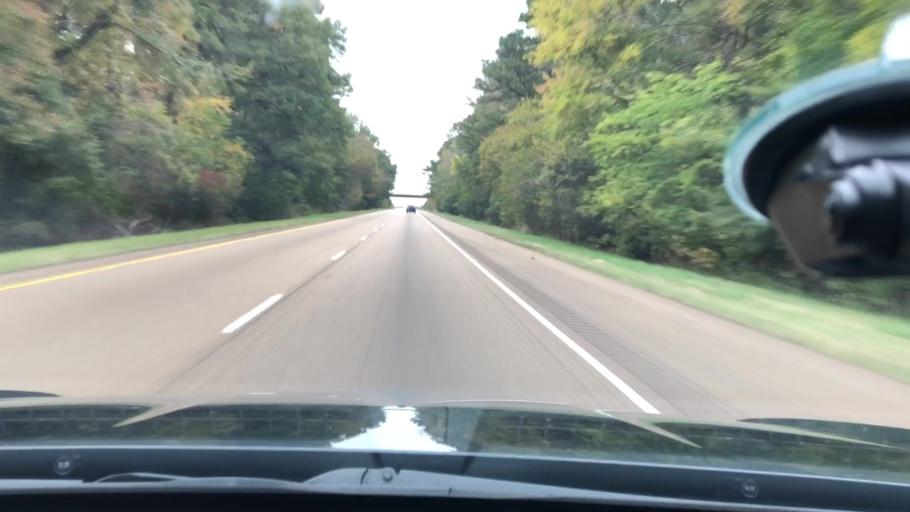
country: US
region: Arkansas
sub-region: Nevada County
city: Prescott
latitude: 33.7745
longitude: -93.4723
